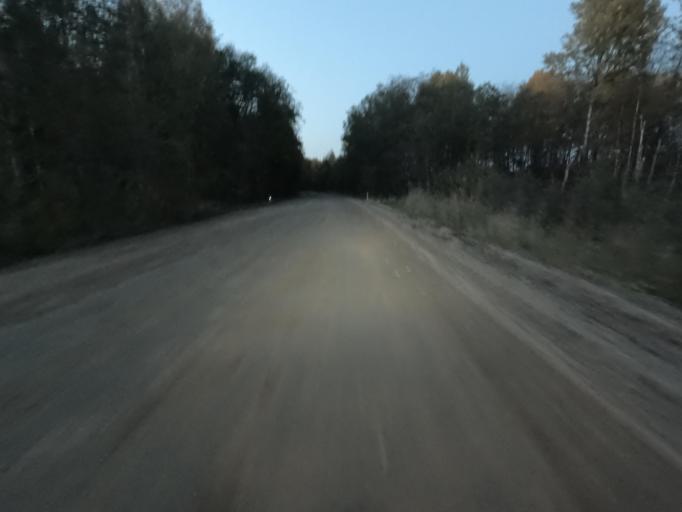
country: RU
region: Leningrad
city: Lyuban'
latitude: 59.1890
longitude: 31.2508
